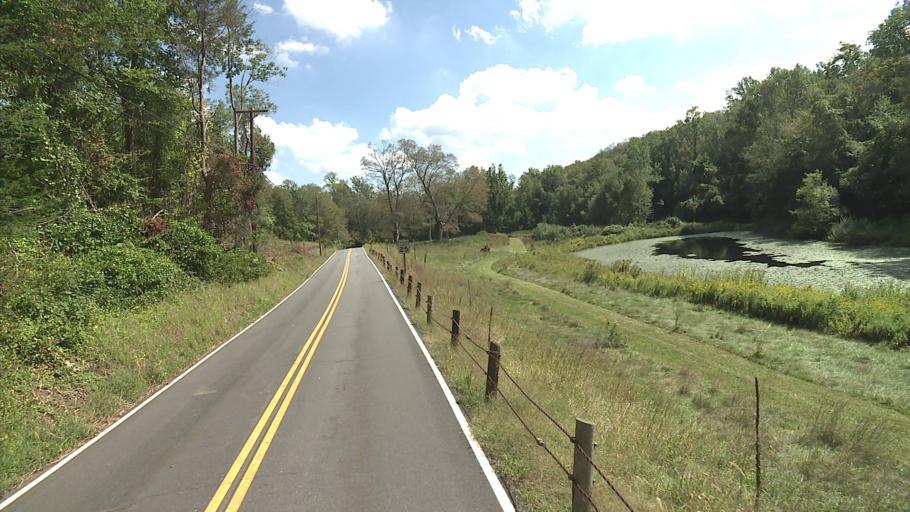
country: US
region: Connecticut
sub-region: Middlesex County
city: Chester Center
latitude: 41.4298
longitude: -72.4263
